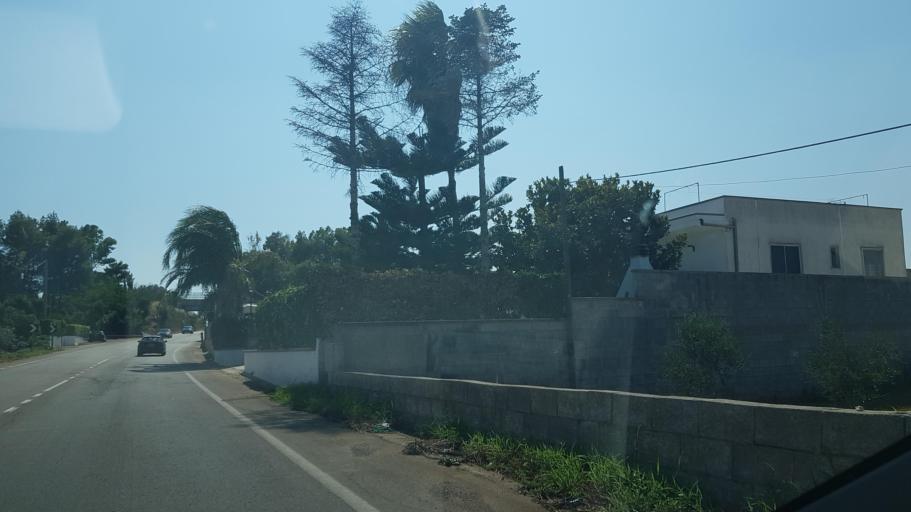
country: IT
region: Apulia
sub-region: Provincia di Lecce
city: Taurisano
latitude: 39.9505
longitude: 18.1998
